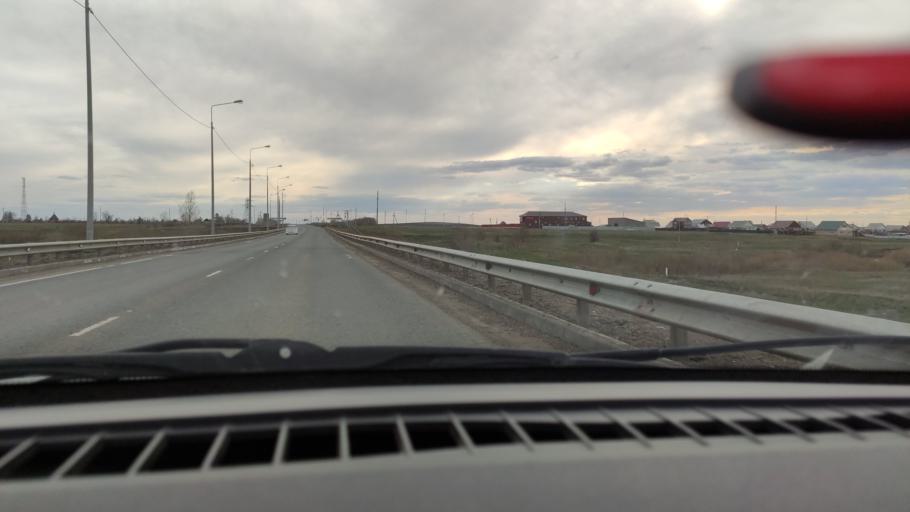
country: RU
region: Orenburg
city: Sakmara
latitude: 52.3314
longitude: 55.5050
